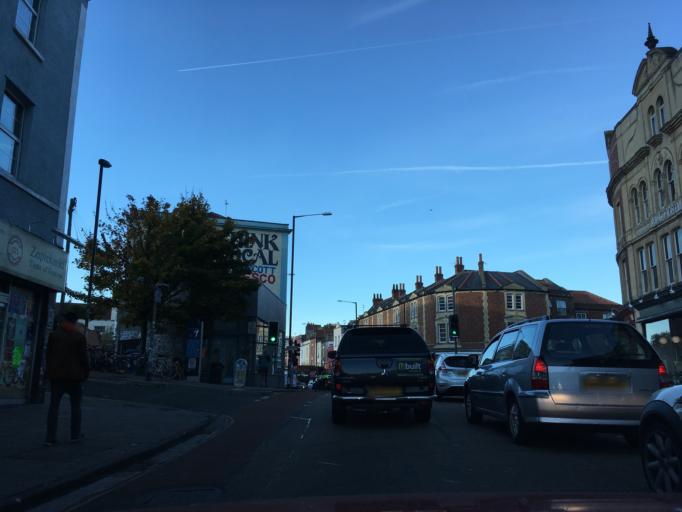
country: GB
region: England
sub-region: Bristol
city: Bristol
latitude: 51.4638
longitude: -2.5898
